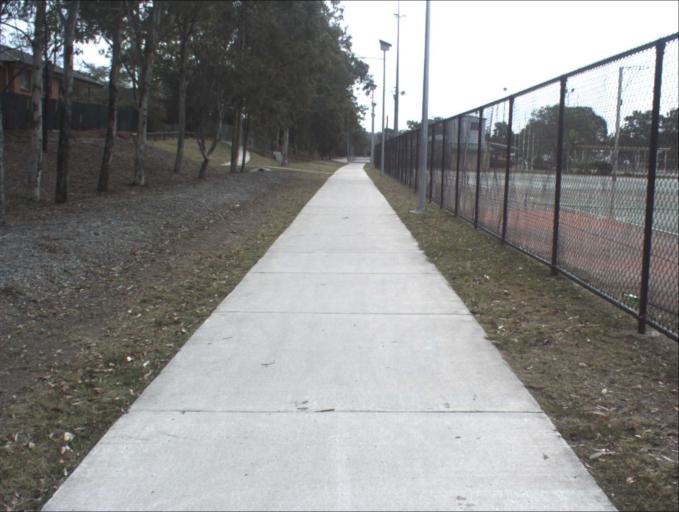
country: AU
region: Queensland
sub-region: Logan
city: Logan City
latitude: -27.6340
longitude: 153.1126
